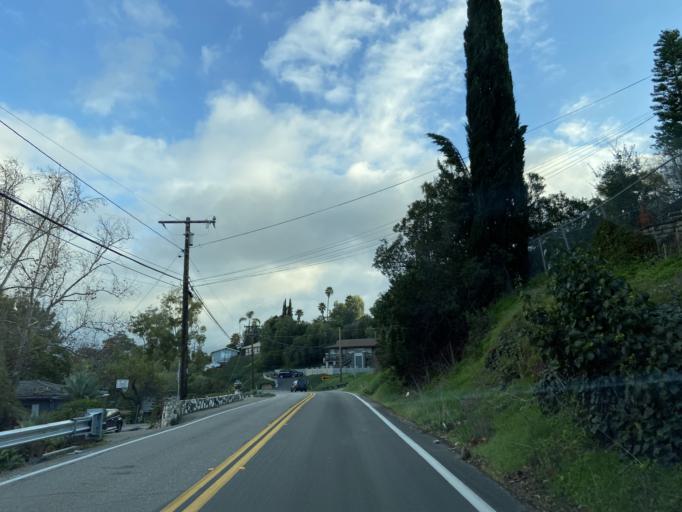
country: US
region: California
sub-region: San Diego County
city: Casa de Oro-Mount Helix
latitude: 32.7725
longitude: -116.9787
